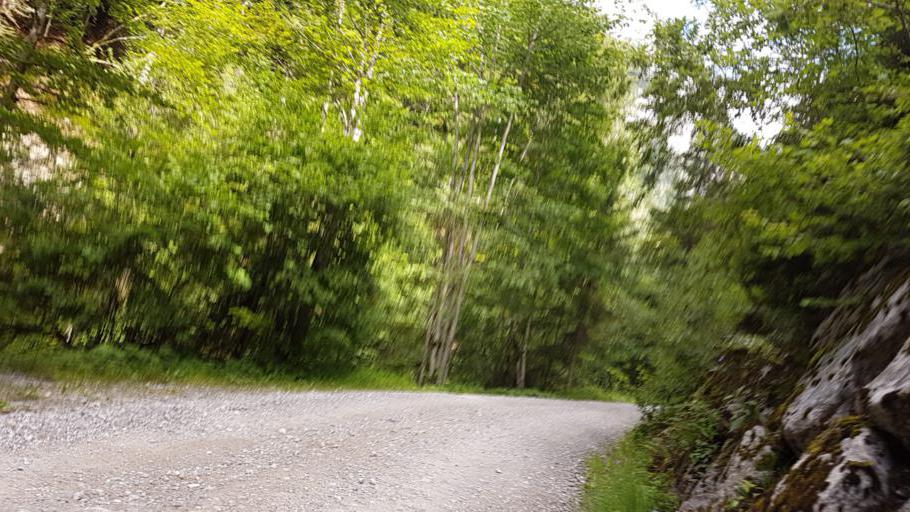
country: CH
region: Bern
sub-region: Obersimmental-Saanen District
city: Boltigen
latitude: 46.6754
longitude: 7.4524
